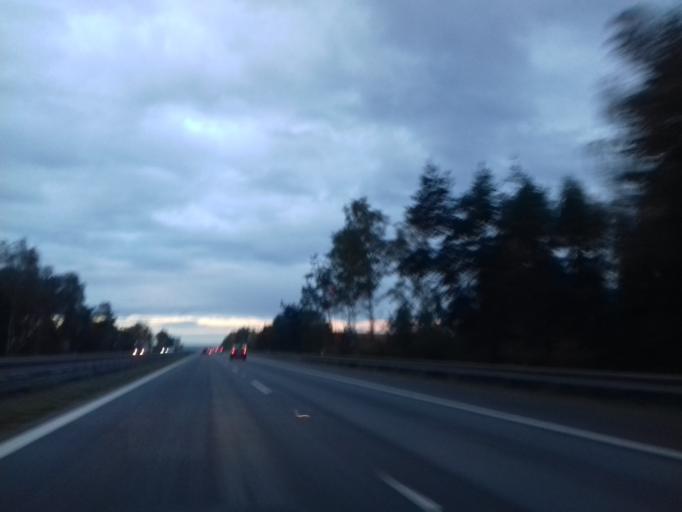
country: CZ
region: Central Bohemia
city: Cechtice
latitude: 49.6419
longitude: 15.1261
